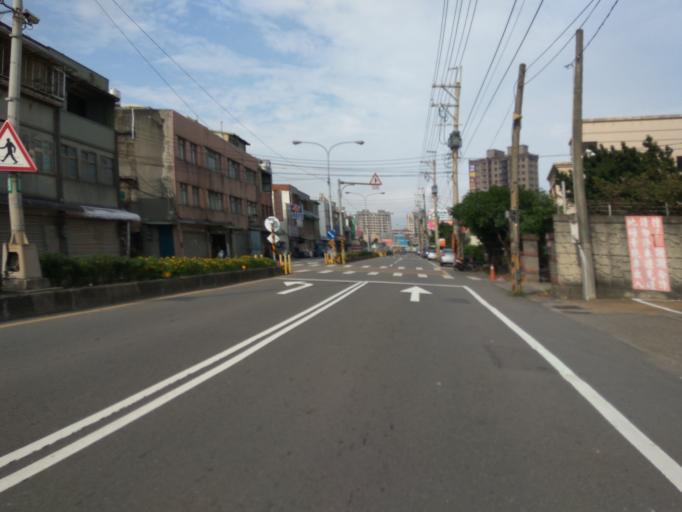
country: TW
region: Taiwan
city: Taoyuan City
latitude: 25.0013
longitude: 121.2163
